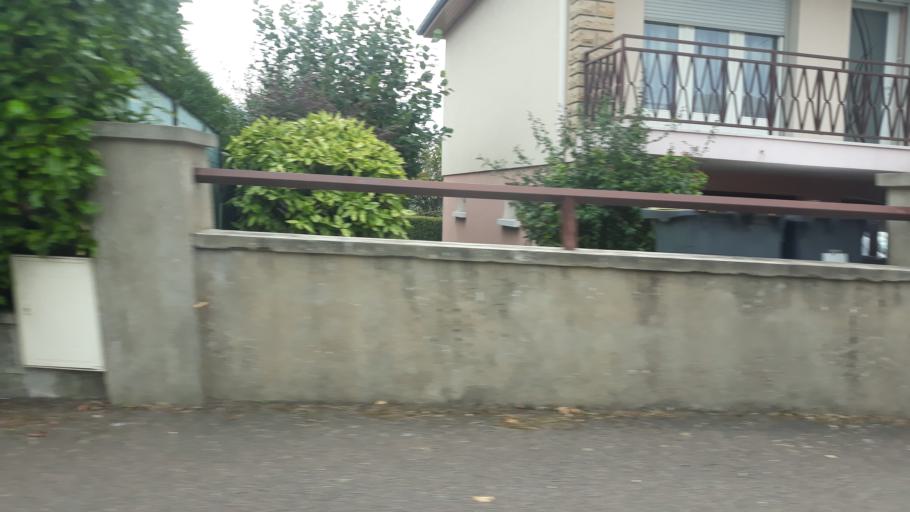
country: FR
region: Bourgogne
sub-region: Departement de Saone-et-Loire
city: Le Creusot
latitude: 46.8134
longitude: 4.4287
